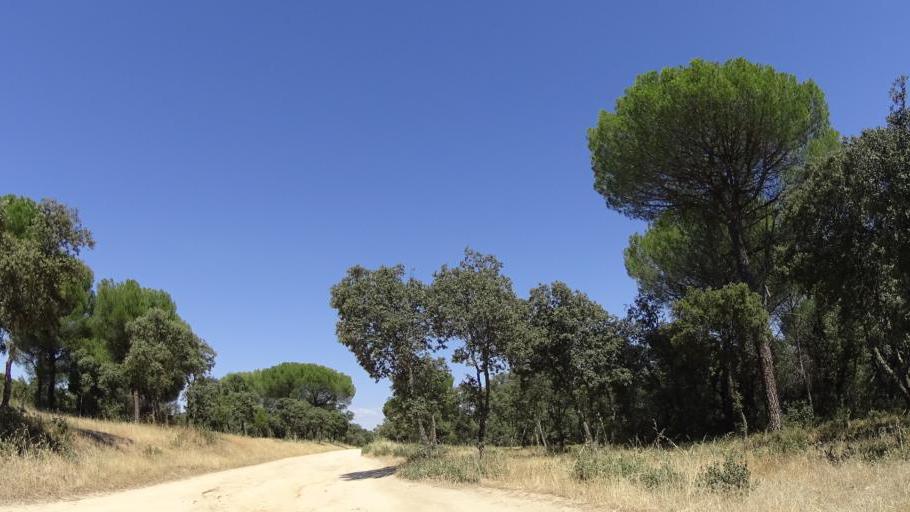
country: ES
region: Madrid
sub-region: Provincia de Madrid
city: Majadahonda
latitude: 40.4390
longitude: -3.8625
